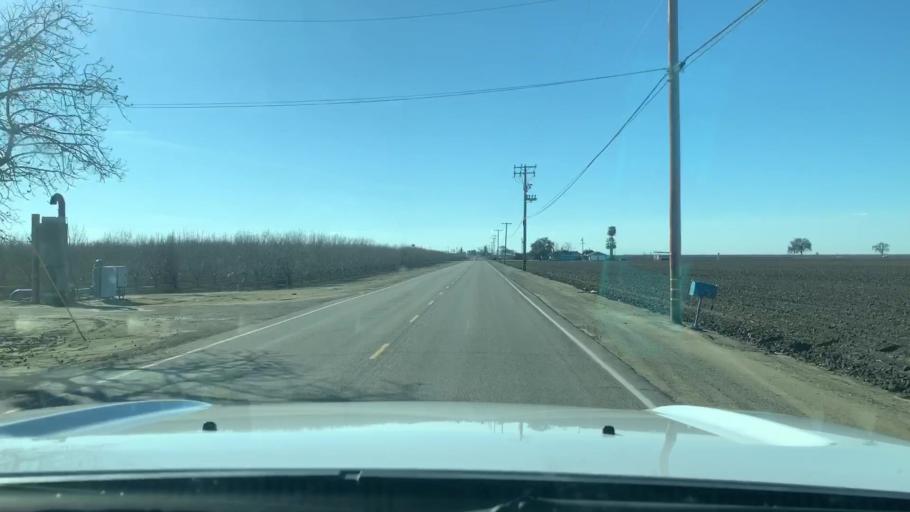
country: US
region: California
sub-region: Tulare County
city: Tulare
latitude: 36.1813
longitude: -119.4492
